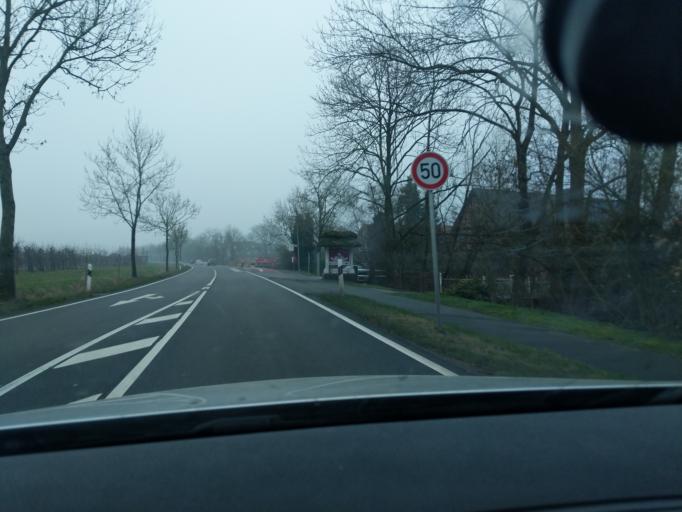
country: DE
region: Lower Saxony
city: Jork
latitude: 53.5500
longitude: 9.6657
